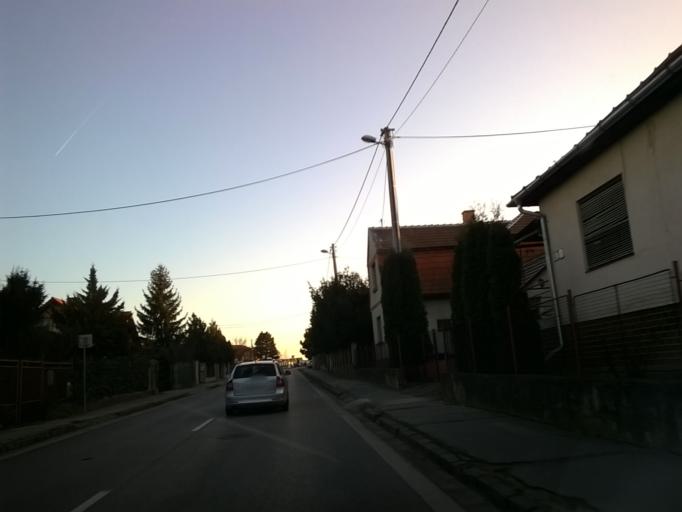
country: SK
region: Nitriansky
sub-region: Okres Nitra
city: Nitra
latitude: 48.2906
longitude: 18.0724
